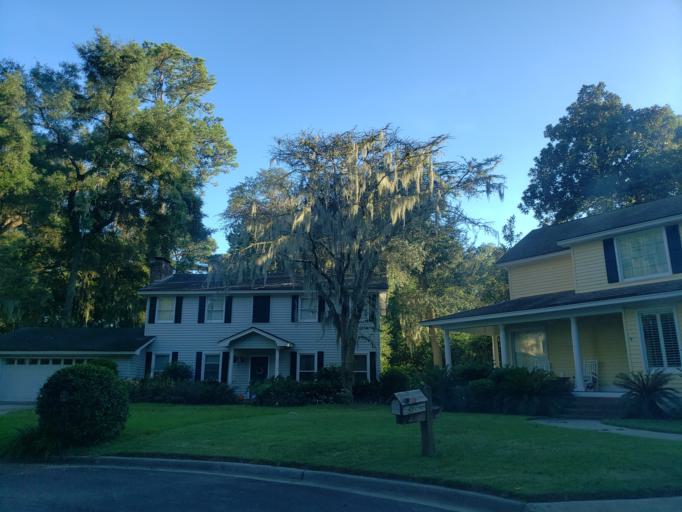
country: US
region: Georgia
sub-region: Chatham County
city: Isle of Hope
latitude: 31.9973
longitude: -81.0633
